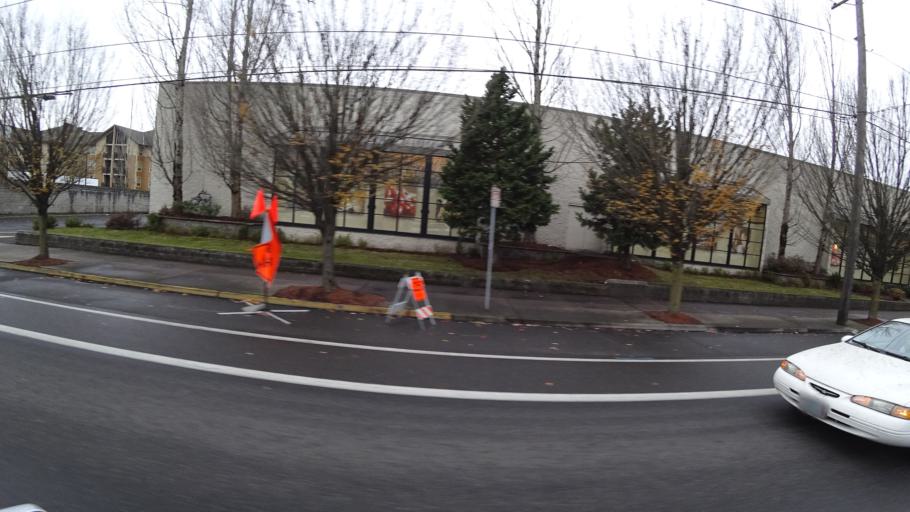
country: US
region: Oregon
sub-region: Multnomah County
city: Lents
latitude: 45.5244
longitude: -122.5378
